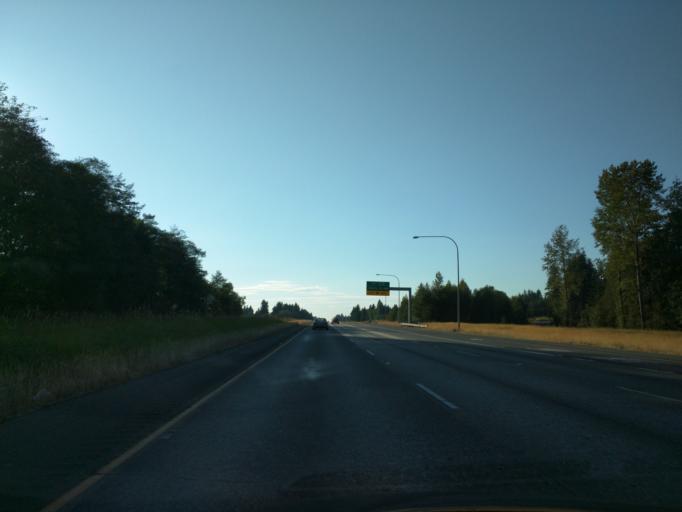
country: US
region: Washington
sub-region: Snohomish County
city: Stanwood
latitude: 48.2644
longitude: -122.2647
